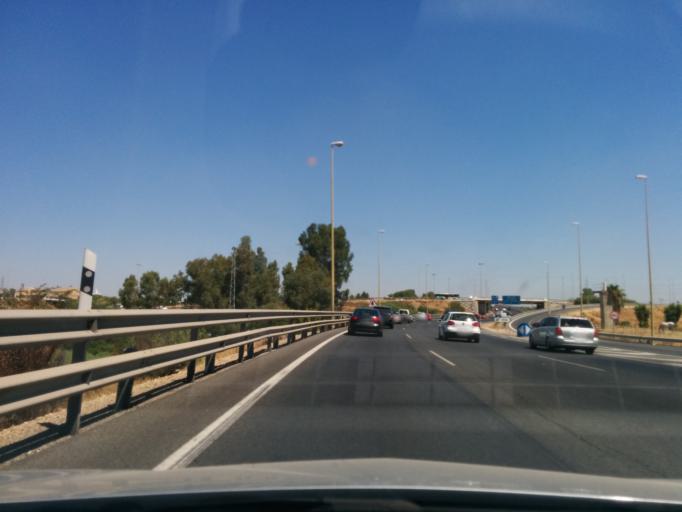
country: ES
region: Andalusia
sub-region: Provincia de Sevilla
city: Camas
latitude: 37.3850
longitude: -6.0256
